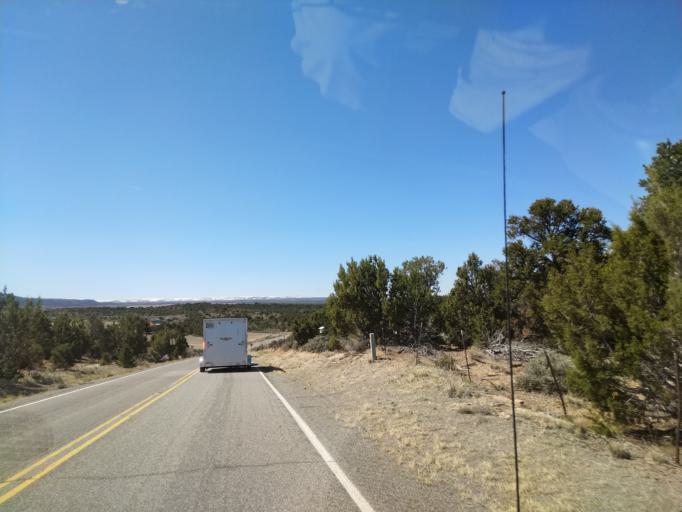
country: US
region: Colorado
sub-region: Mesa County
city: Redlands
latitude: 38.9964
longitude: -108.7155
